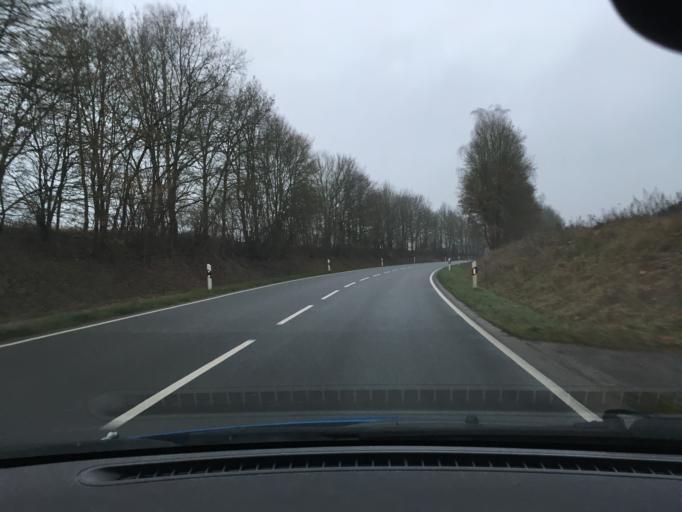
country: DE
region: Lower Saxony
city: Oldendorf
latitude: 53.1441
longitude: 10.2112
